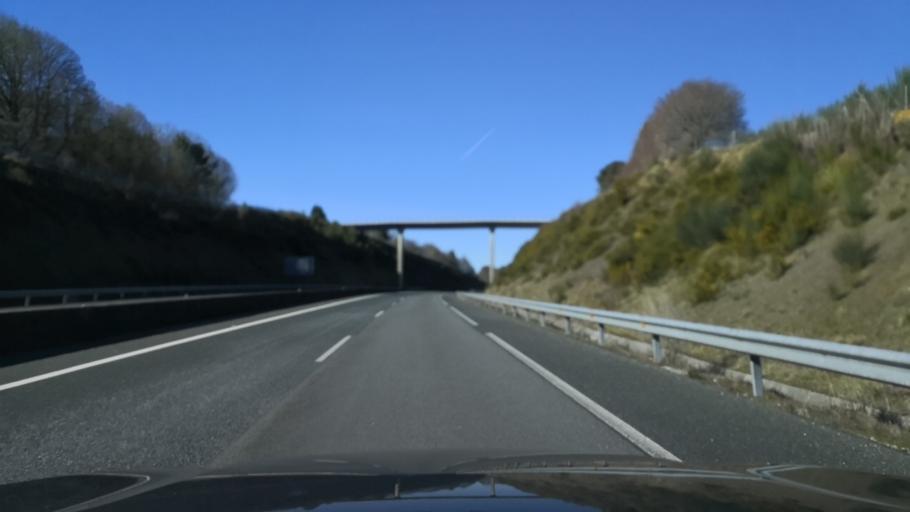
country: ES
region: Galicia
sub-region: Provincia de Pontevedra
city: Lalin
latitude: 42.6495
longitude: -8.1356
